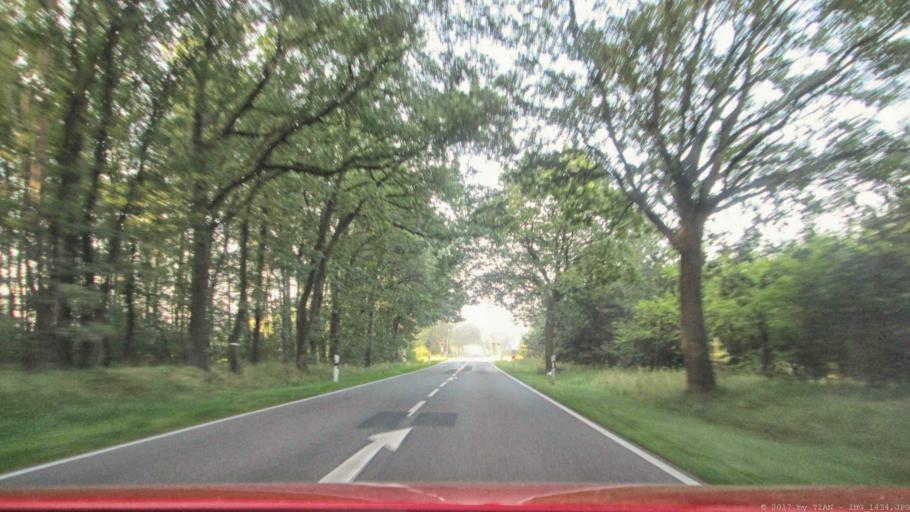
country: DE
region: Lower Saxony
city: Wittingen
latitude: 52.7712
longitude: 10.7121
